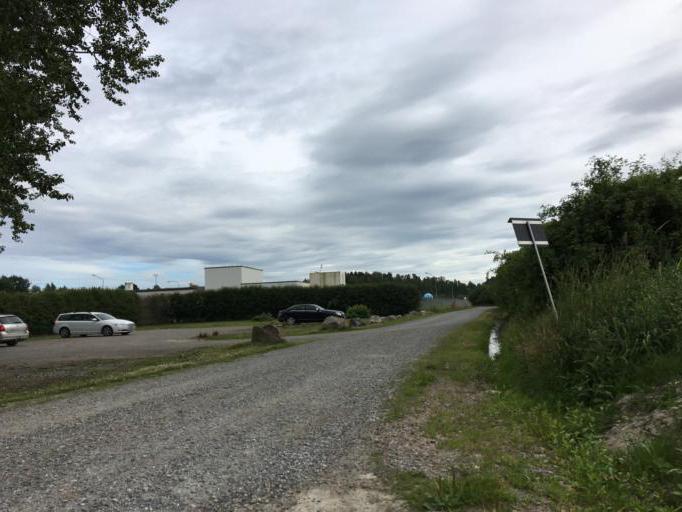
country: SE
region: Soedermanland
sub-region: Eskilstuna Kommun
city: Torshalla
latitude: 59.3884
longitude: 16.4584
